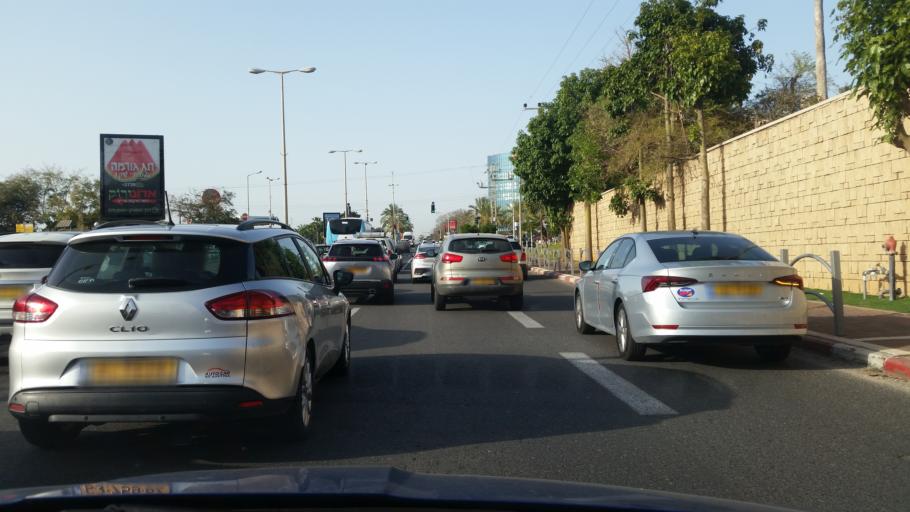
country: IL
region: Central District
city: Ra'anana
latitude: 32.1840
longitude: 34.8537
